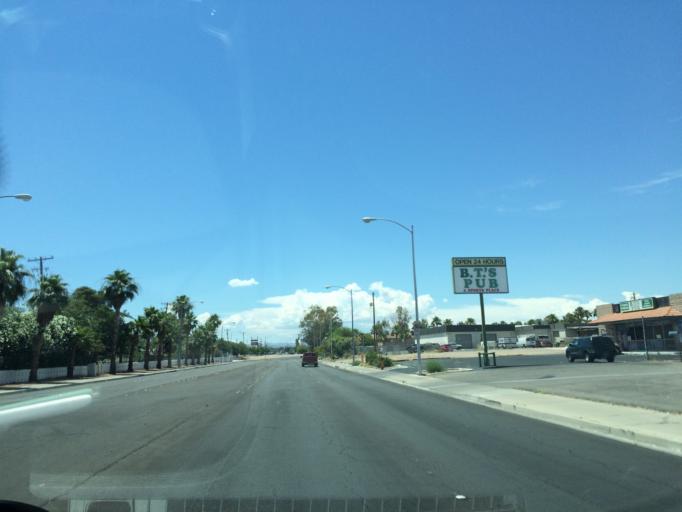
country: US
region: Nevada
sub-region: Clark County
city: Winchester
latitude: 36.1541
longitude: -115.1011
